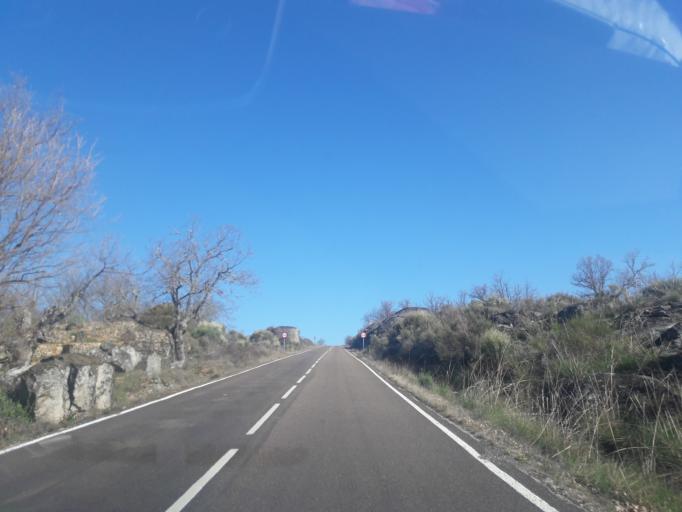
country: ES
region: Castille and Leon
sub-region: Provincia de Salamanca
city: Cabeza del Caballo
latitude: 41.1002
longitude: -6.5534
